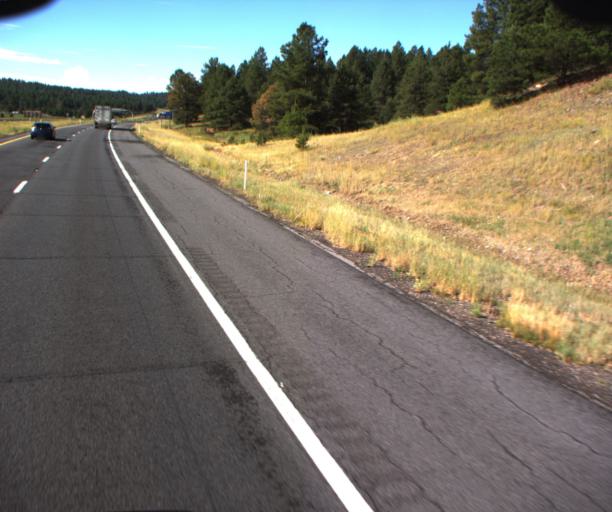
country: US
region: Arizona
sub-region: Coconino County
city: Kachina Village
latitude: 35.1050
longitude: -111.6814
